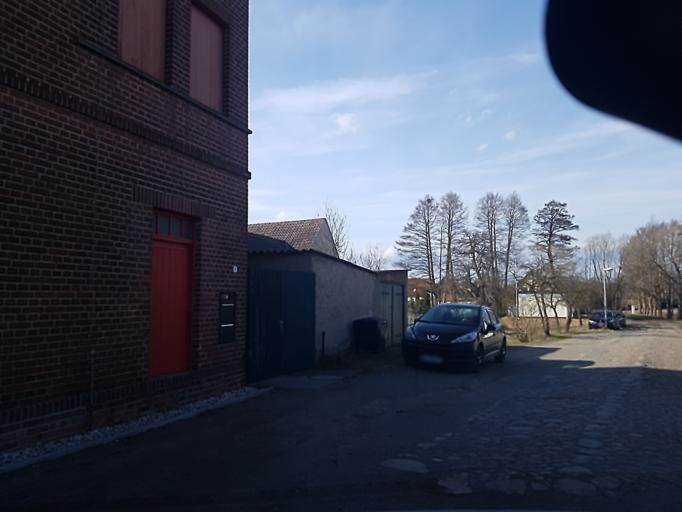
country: DE
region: Brandenburg
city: Schonewalde
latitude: 51.6366
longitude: 13.6055
